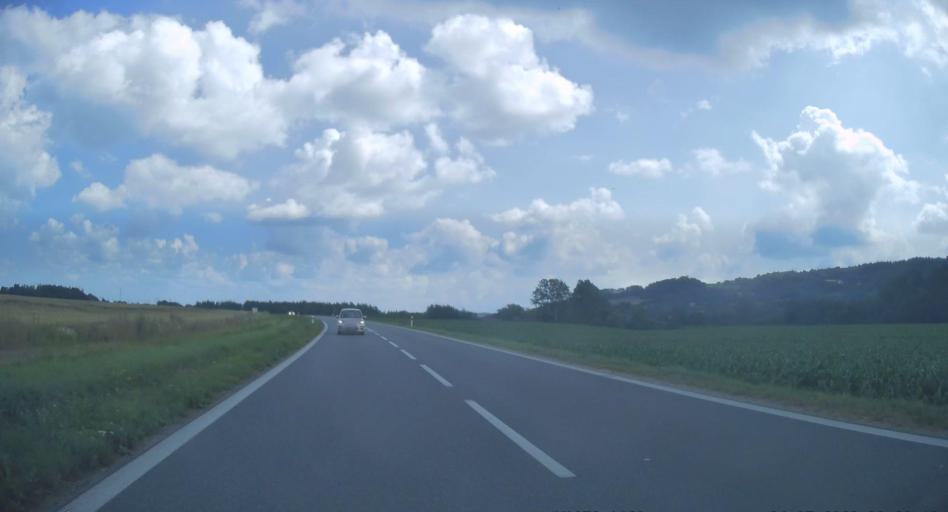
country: PL
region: Lesser Poland Voivodeship
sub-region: Powiat tarnowski
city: Wielka Wies
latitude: 49.9306
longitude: 20.8422
